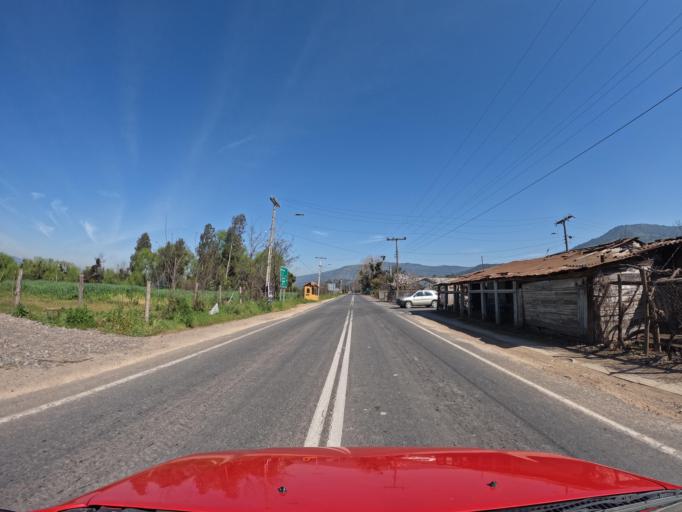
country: CL
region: Maule
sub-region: Provincia de Curico
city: Rauco
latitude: -34.9793
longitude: -71.4003
